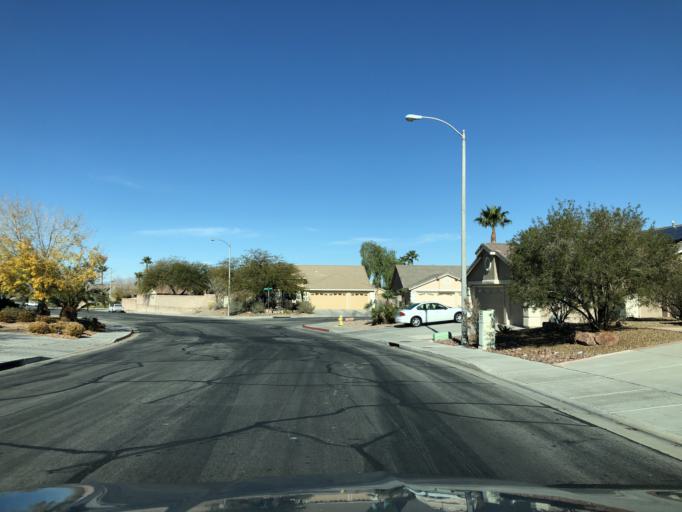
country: US
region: Nevada
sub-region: Clark County
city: Whitney
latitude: 36.0086
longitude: -115.0899
